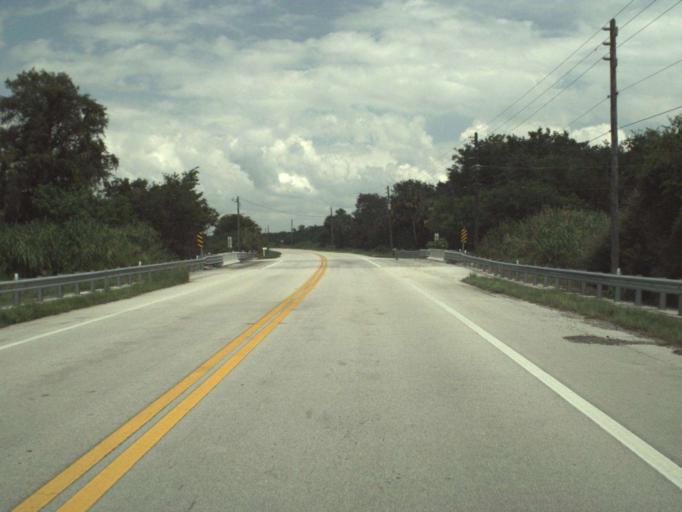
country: US
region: Florida
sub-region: Okeechobee County
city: Taylor Creek
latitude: 27.1104
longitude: -80.6635
